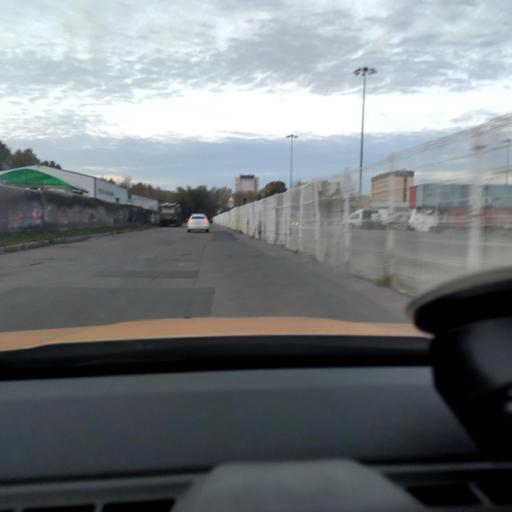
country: RU
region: Moscow
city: Yaroslavskiy
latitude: 55.8651
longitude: 37.7063
